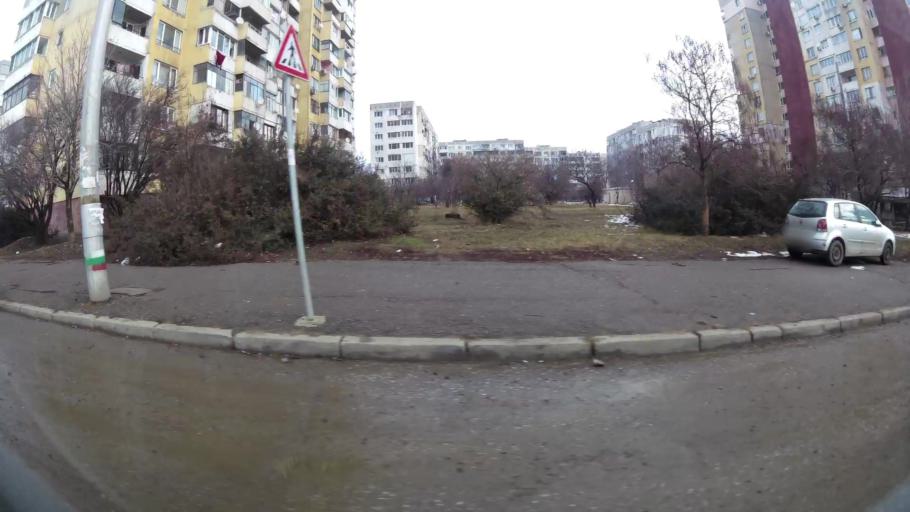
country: BG
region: Sofiya
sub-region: Obshtina Bozhurishte
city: Bozhurishte
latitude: 42.7111
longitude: 23.2427
